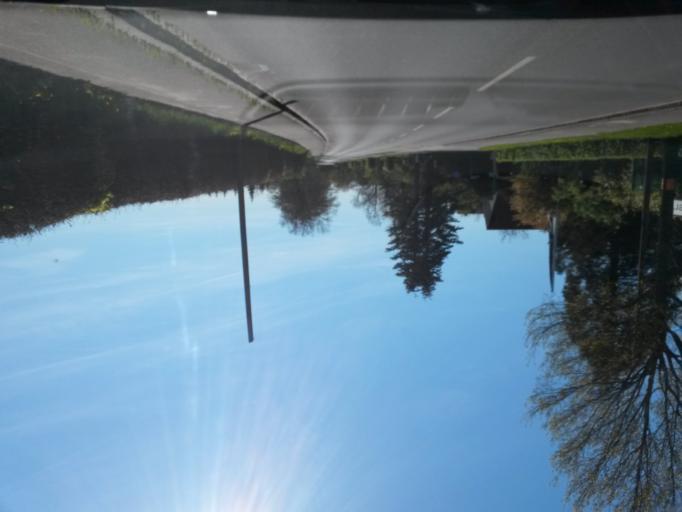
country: DE
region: Schleswig-Holstein
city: Rellingen
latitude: 53.6205
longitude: 9.8223
